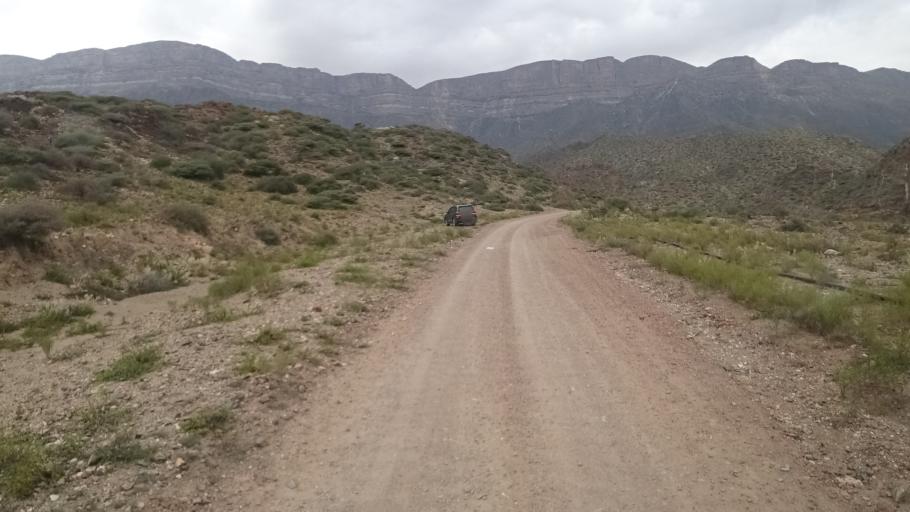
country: OM
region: Zufar
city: Salalah
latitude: 17.1734
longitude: 54.9507
